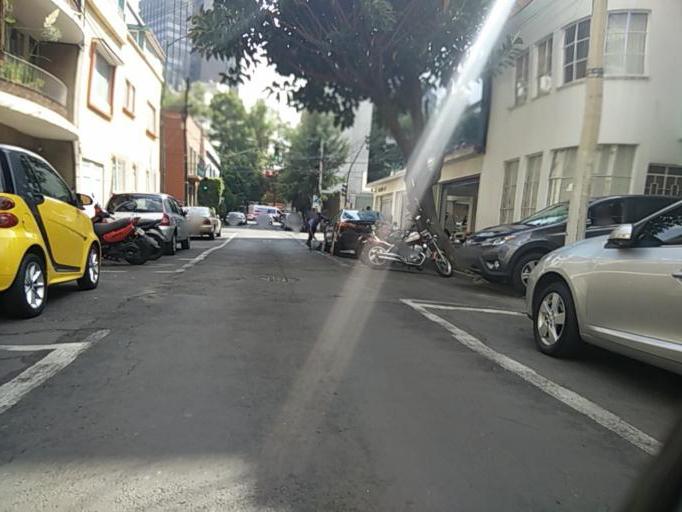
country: MX
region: Mexico City
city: Miguel Hidalgo
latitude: 19.4346
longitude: -99.1815
